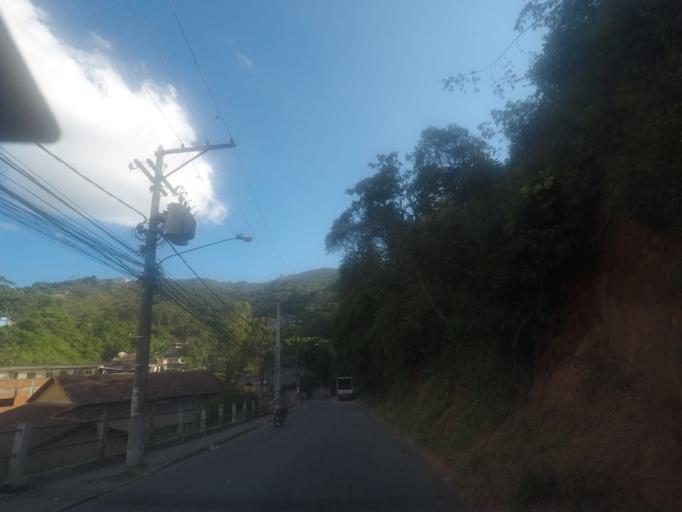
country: BR
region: Rio de Janeiro
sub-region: Petropolis
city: Petropolis
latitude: -22.5050
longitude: -43.1545
